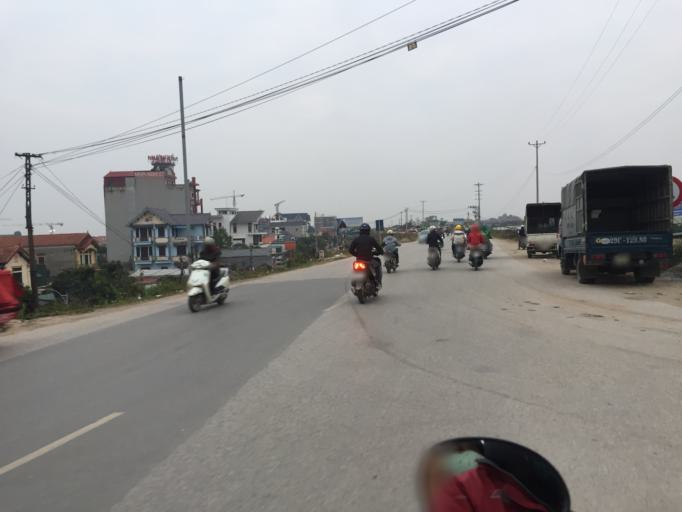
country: VN
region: Hung Yen
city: Van Giang
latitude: 20.9707
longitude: 105.9195
